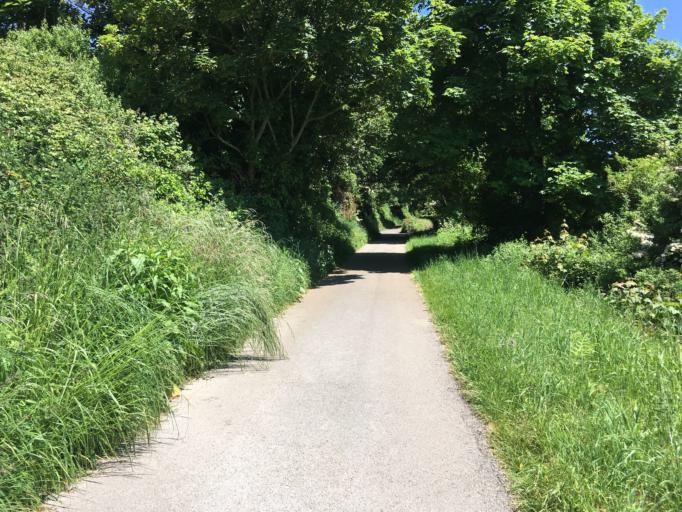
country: GB
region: England
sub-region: Devon
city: Dartmouth
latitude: 50.3449
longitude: -3.5570
